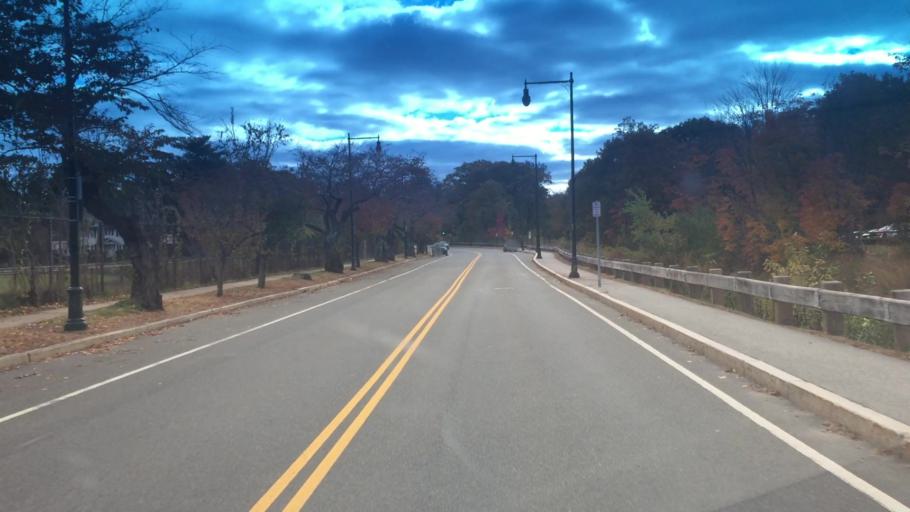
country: US
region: Massachusetts
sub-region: Middlesex County
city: Winchester
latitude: 42.4496
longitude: -71.1376
